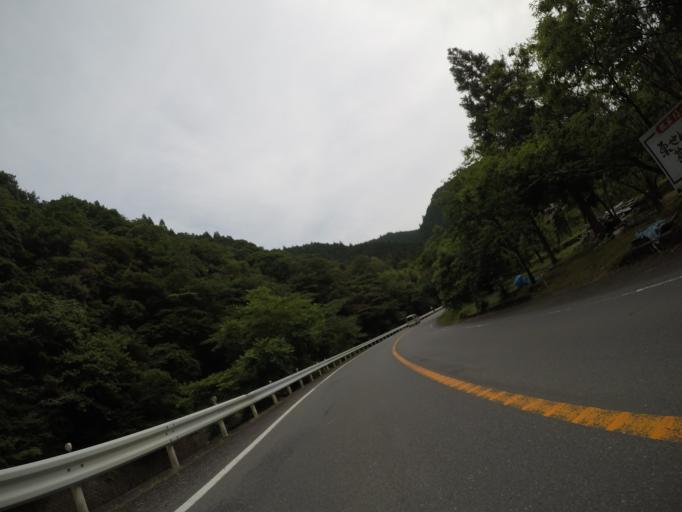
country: JP
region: Shizuoka
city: Fujinomiya
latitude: 35.1967
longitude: 138.5394
